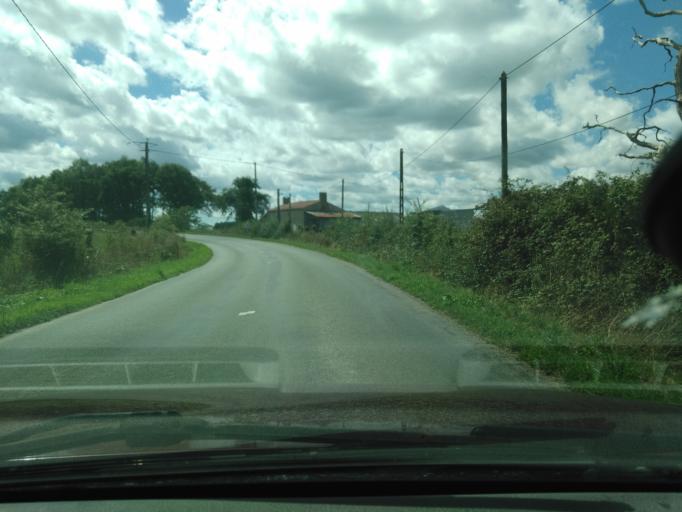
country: FR
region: Pays de la Loire
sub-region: Departement de la Vendee
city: La Ferriere
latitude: 46.7411
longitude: -1.3116
